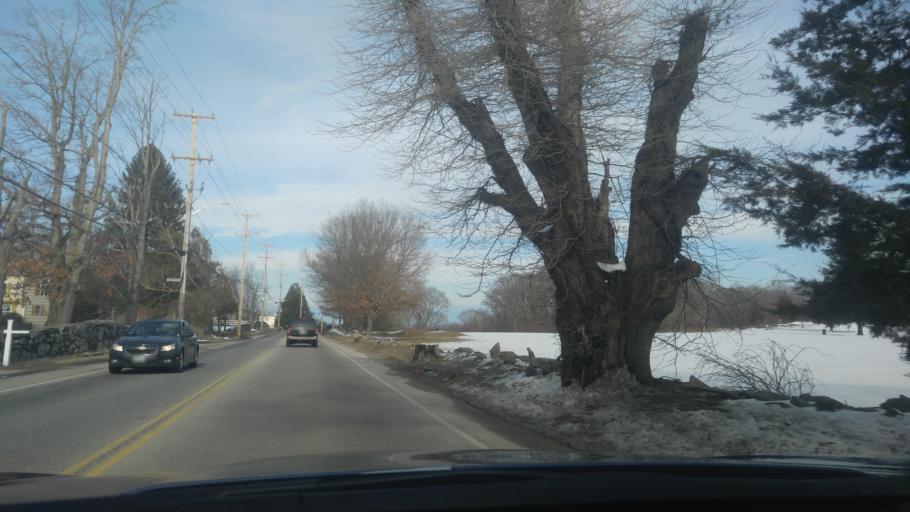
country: US
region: Rhode Island
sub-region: Kent County
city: West Warwick
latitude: 41.7071
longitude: -71.5120
